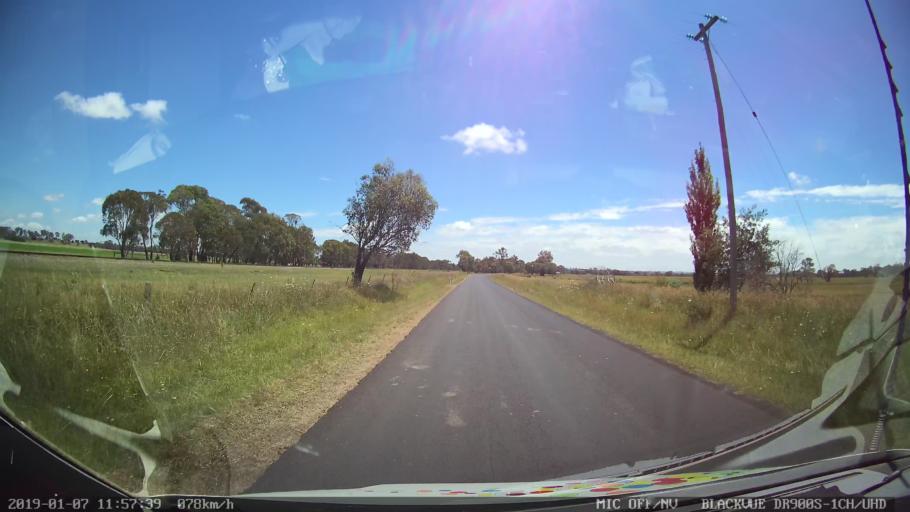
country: AU
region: New South Wales
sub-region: Guyra
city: Guyra
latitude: -30.2620
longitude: 151.6657
